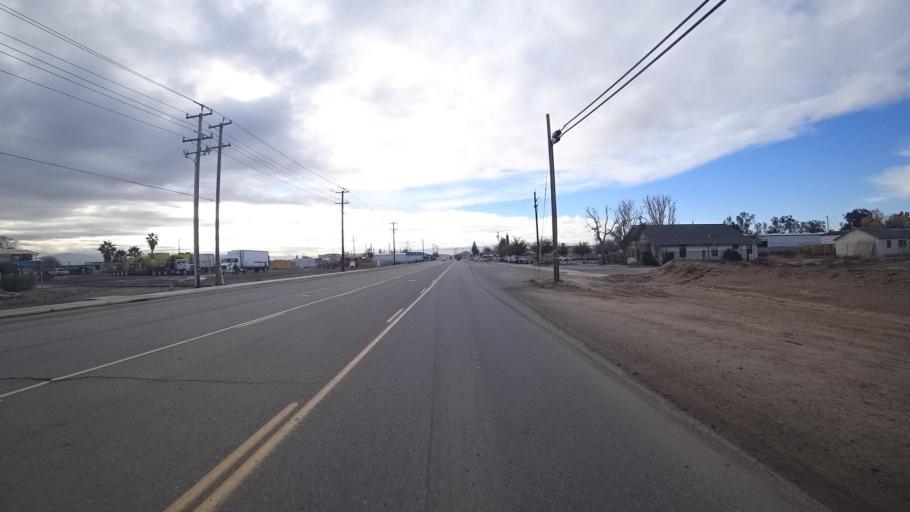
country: US
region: California
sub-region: Kern County
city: Greenacres
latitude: 35.3887
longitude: -119.0744
